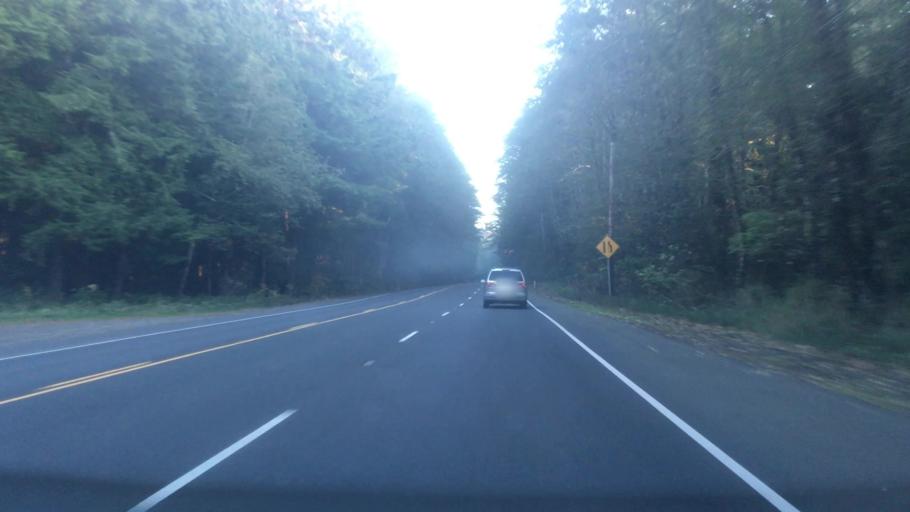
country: US
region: Oregon
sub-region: Clatsop County
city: Cannon Beach
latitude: 45.7885
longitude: -123.9594
